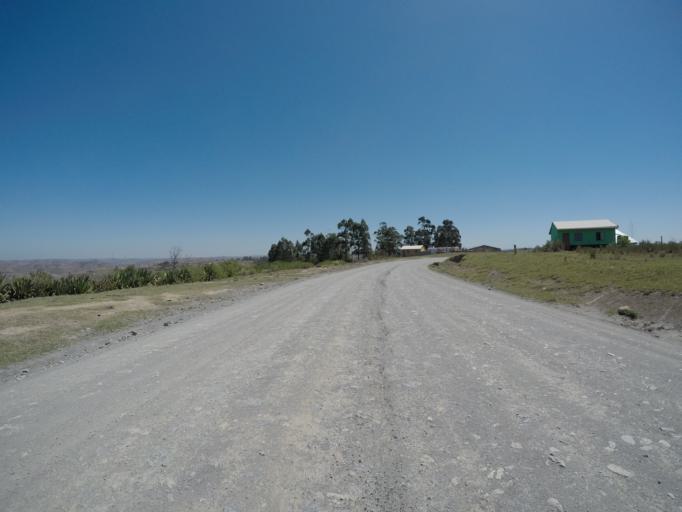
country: ZA
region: Eastern Cape
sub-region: OR Tambo District Municipality
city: Libode
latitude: -31.9739
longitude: 29.0321
